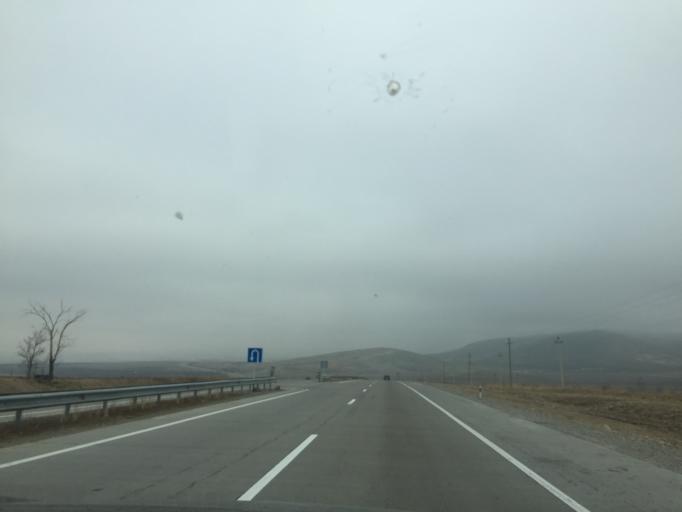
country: KZ
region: Ongtustik Qazaqstan
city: Sastobe
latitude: 42.5216
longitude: 70.0018
